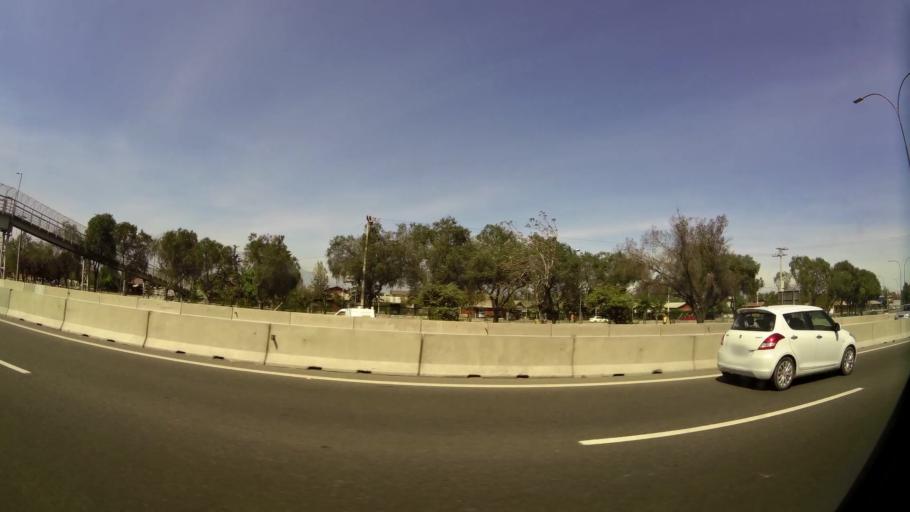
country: CL
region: Santiago Metropolitan
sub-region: Provincia de Maipo
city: San Bernardo
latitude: -33.5367
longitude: -70.6842
